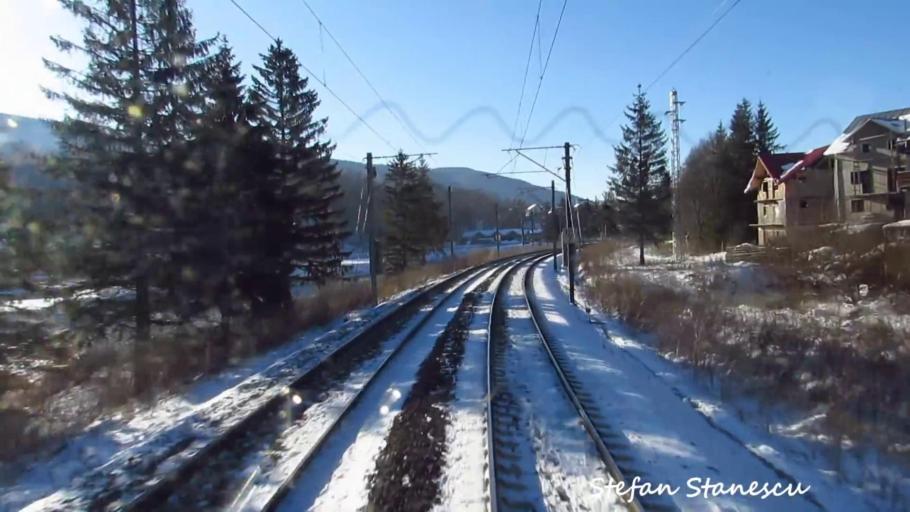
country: RO
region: Prahova
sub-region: Oras Busteni
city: Poiana Tapului
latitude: 45.3847
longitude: 25.5404
